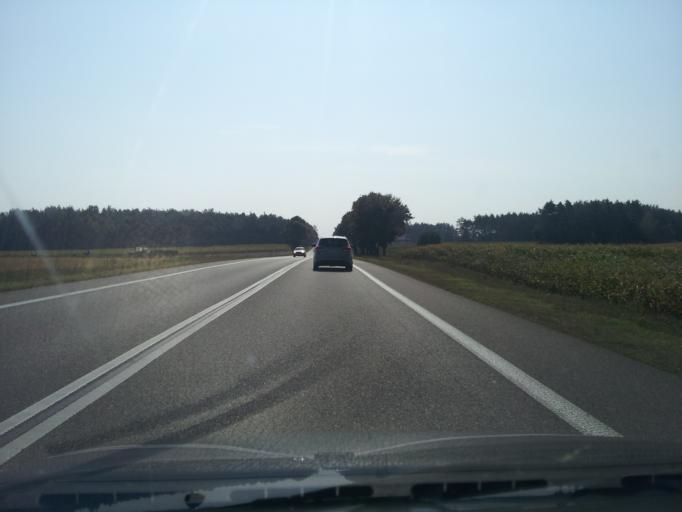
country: PL
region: Masovian Voivodeship
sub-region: Powiat plocki
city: Starozreby
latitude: 52.6688
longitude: 20.0710
